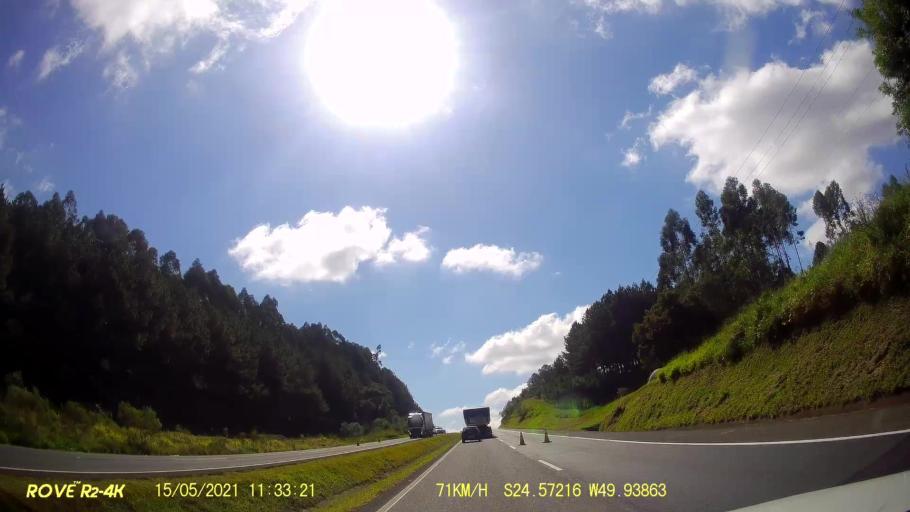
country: BR
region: Parana
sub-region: Pirai Do Sul
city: Pirai do Sul
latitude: -24.5722
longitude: -49.9387
